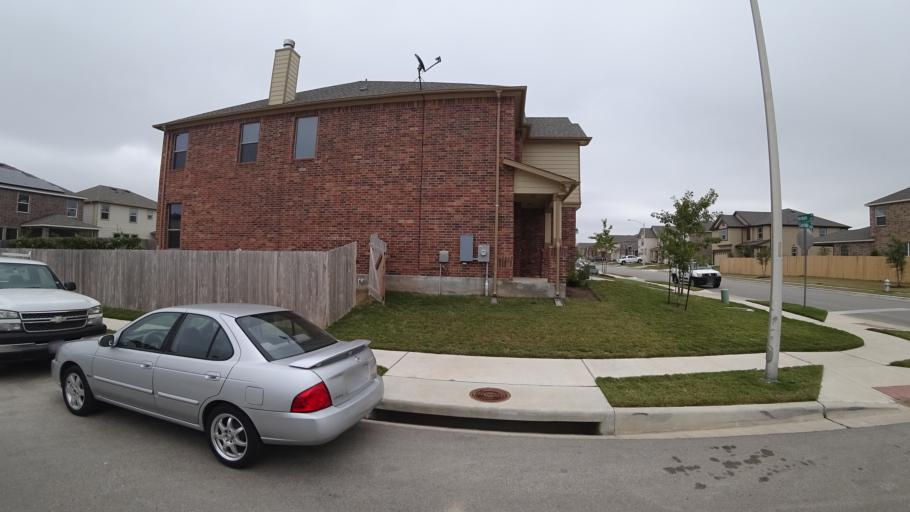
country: US
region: Texas
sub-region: Travis County
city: Pflugerville
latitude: 30.3952
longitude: -97.6499
